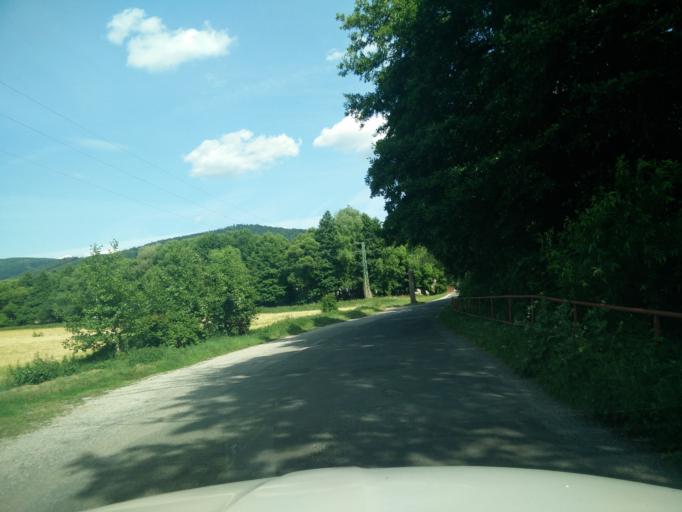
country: SK
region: Nitriansky
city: Prievidza
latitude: 48.8550
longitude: 18.6439
